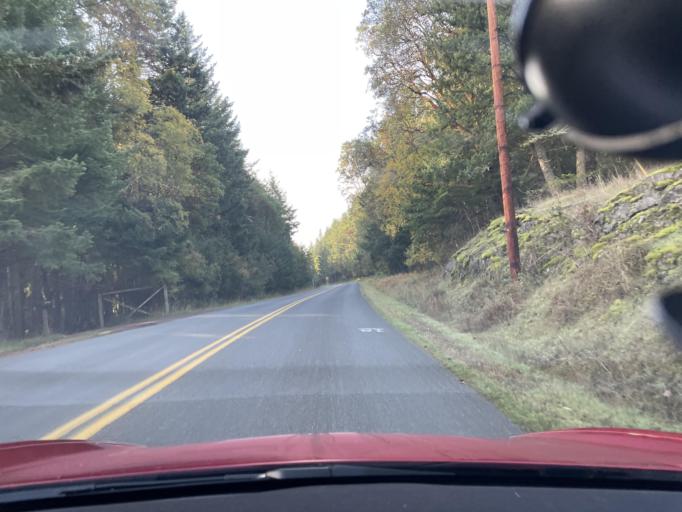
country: US
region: Washington
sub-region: San Juan County
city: Friday Harbor
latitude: 48.5582
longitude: -123.1643
